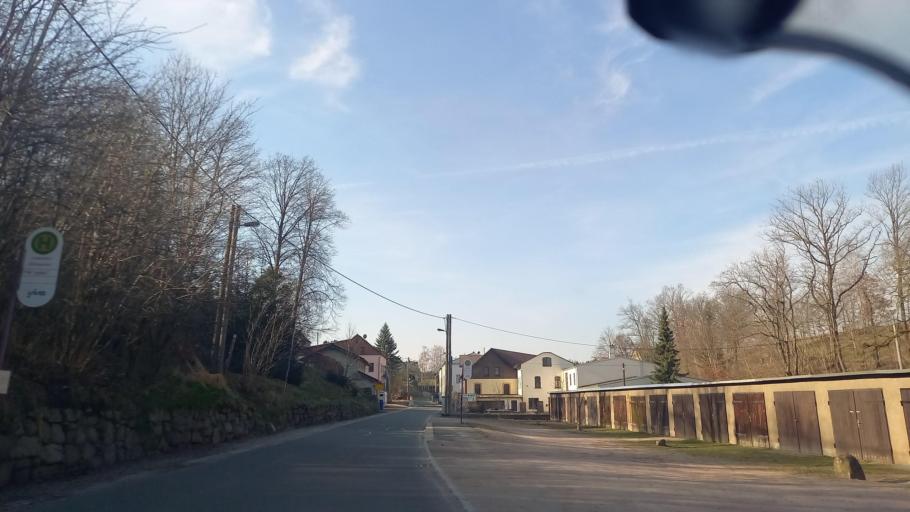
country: DE
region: Saxony
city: Kirchberg
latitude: 50.6150
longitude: 12.5216
